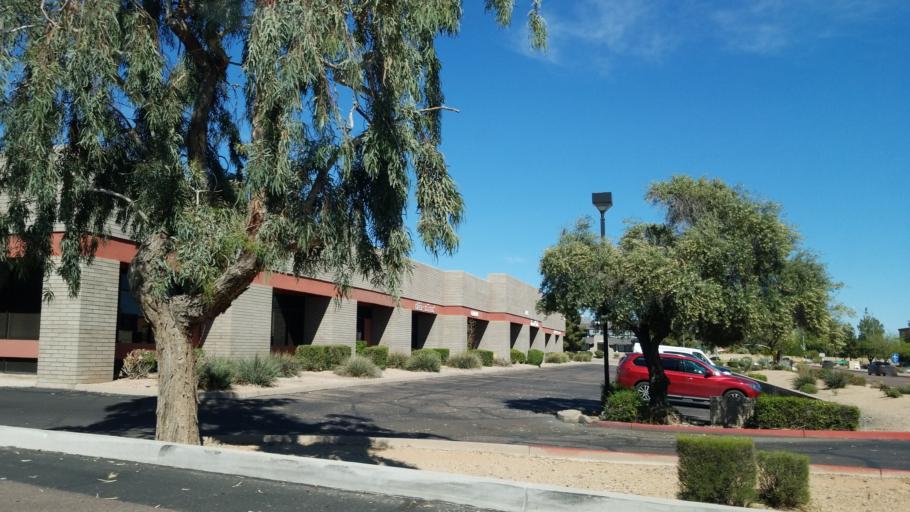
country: US
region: Arizona
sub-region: Maricopa County
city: Paradise Valley
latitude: 33.6141
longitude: -111.9114
